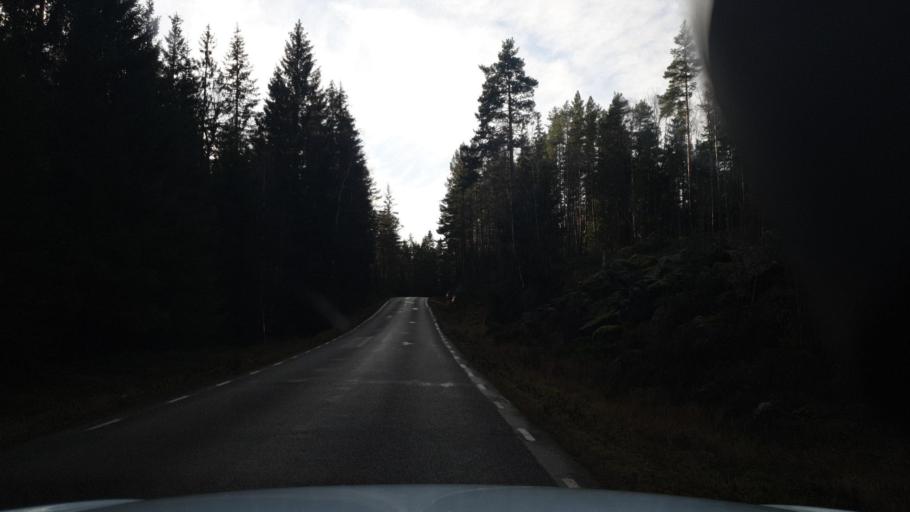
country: NO
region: Hedmark
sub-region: Eidskog
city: Skotterud
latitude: 59.8069
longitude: 12.0459
